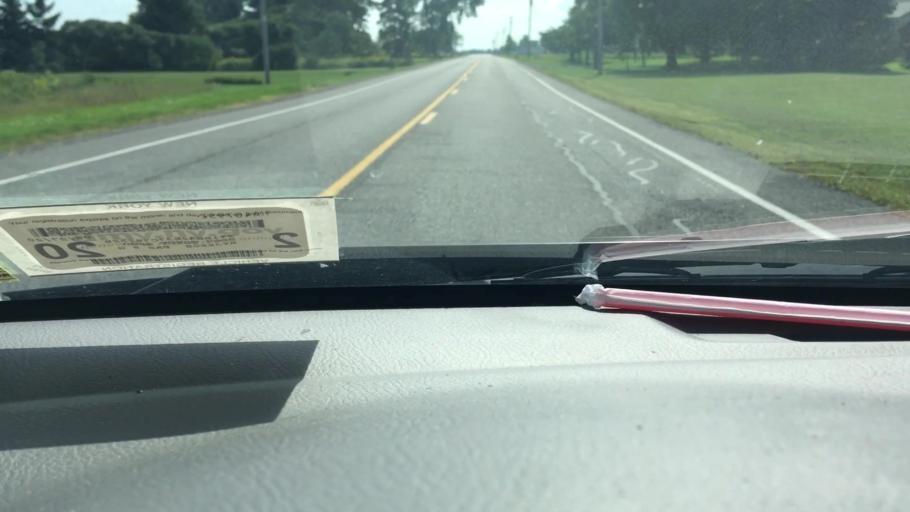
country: US
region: New York
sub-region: Genesee County
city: Batavia
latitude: 43.0367
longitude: -78.1480
